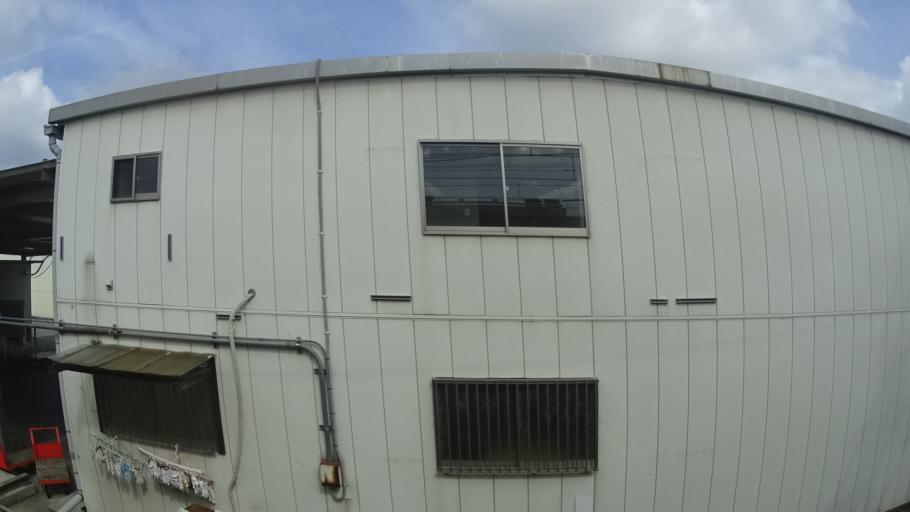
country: JP
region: Tochigi
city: Utsunomiya-shi
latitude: 36.5460
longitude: 139.8886
